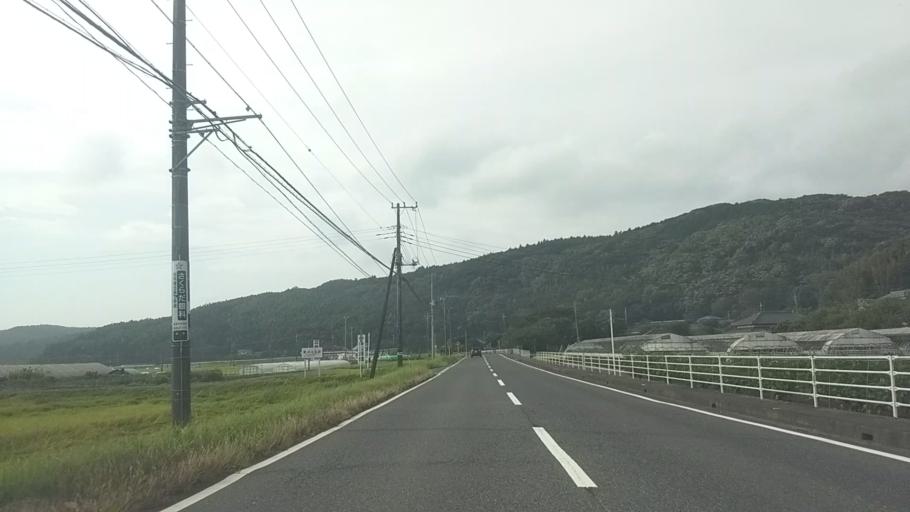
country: JP
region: Chiba
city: Kisarazu
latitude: 35.3067
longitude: 139.9774
